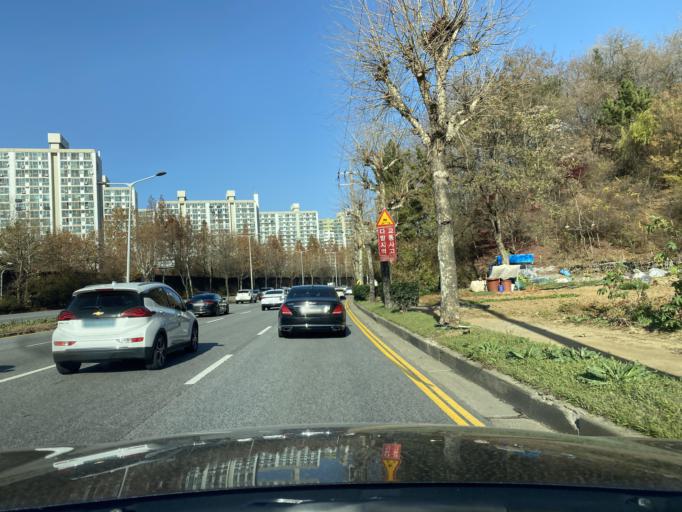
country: KR
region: Incheon
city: Incheon
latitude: 37.4383
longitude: 126.7399
